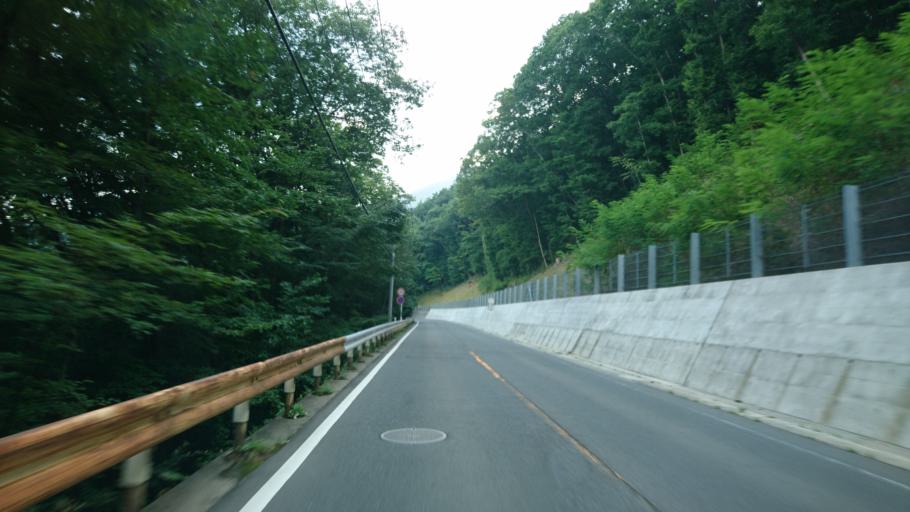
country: JP
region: Gunma
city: Numata
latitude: 36.7212
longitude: 139.2168
